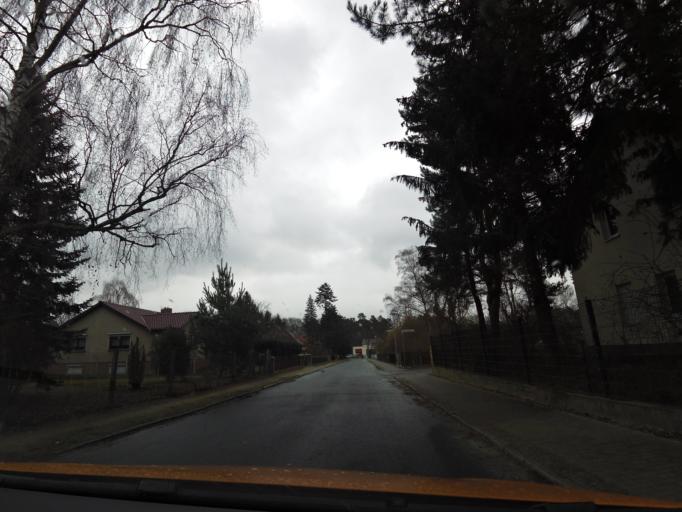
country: DE
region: Brandenburg
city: Rangsdorf
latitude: 52.3289
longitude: 13.4055
